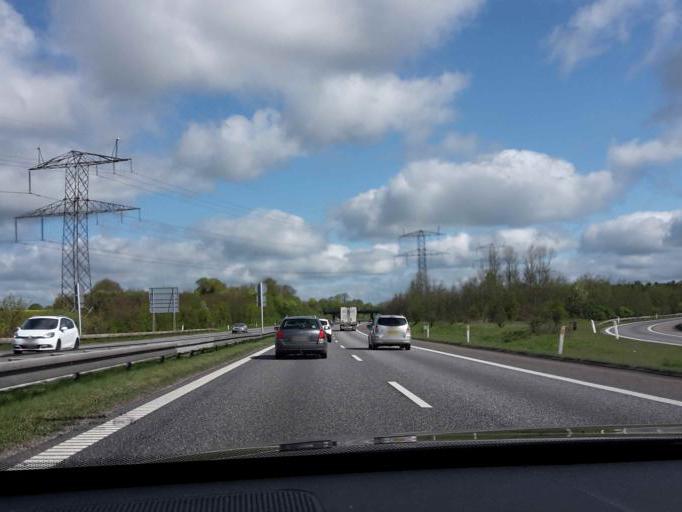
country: DK
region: Central Jutland
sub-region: Arhus Kommune
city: Sabro
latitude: 56.1874
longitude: 10.0702
